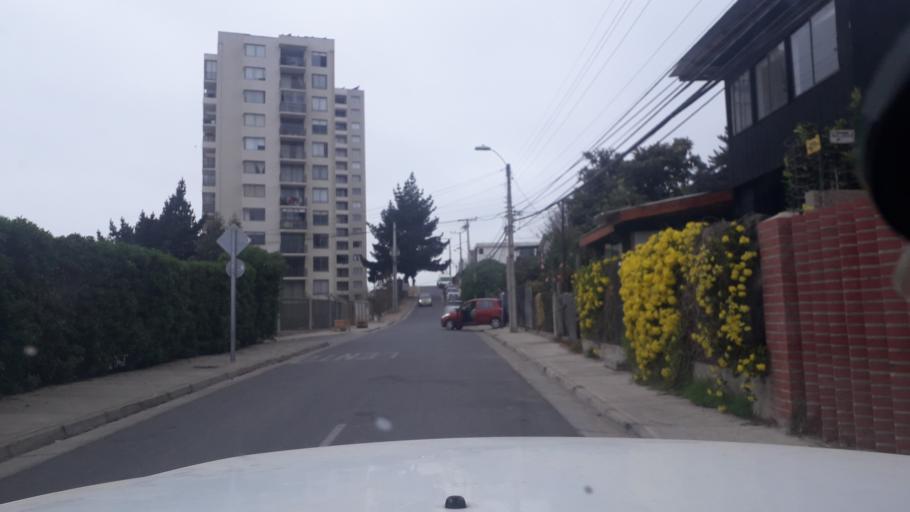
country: CL
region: Valparaiso
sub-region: Provincia de Valparaiso
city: Vina del Mar
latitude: -32.9381
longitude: -71.5350
